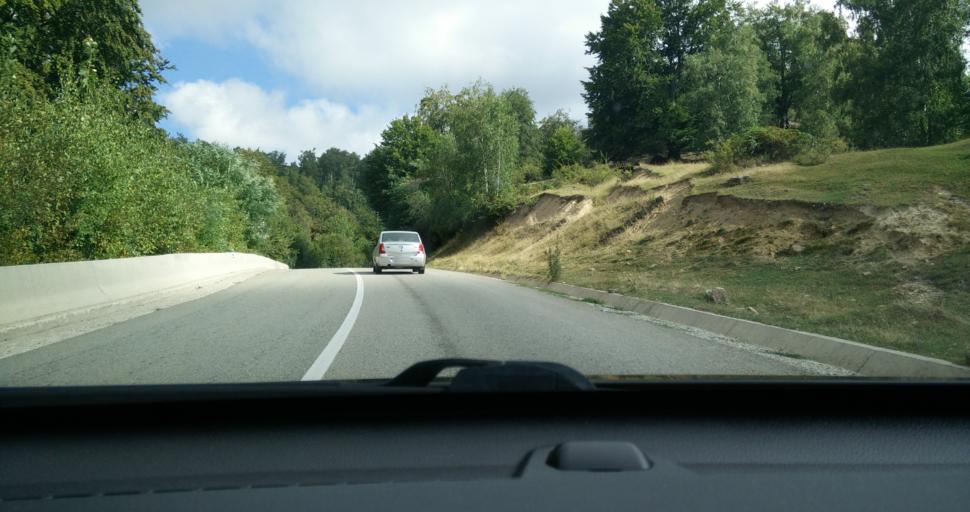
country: RO
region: Gorj
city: Novaci-Straini
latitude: 45.2059
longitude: 23.6983
